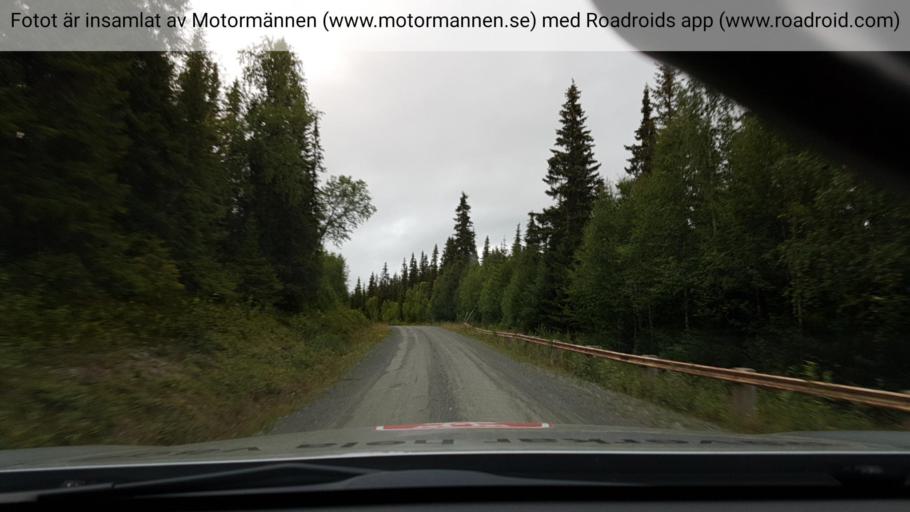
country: SE
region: Vaesterbotten
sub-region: Vilhelmina Kommun
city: Sjoberg
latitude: 65.5387
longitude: 15.4315
